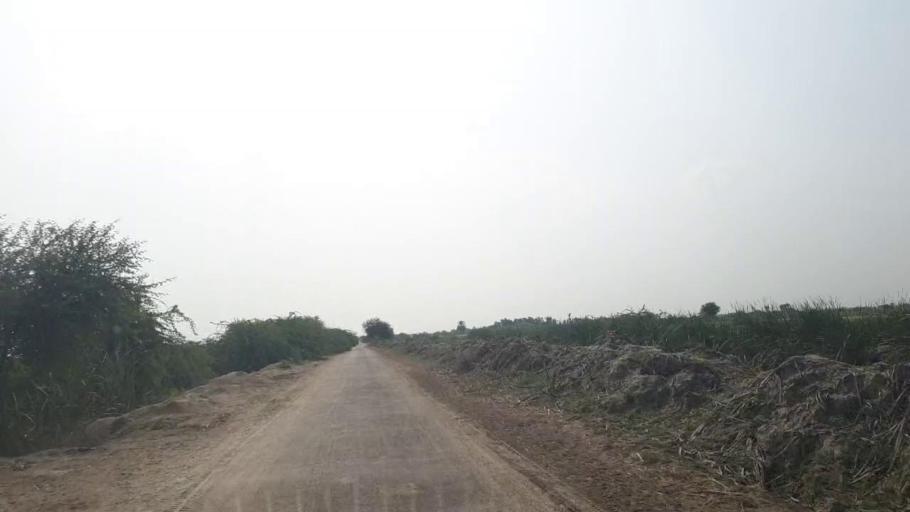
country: PK
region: Sindh
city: Badin
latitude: 24.7226
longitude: 68.7347
